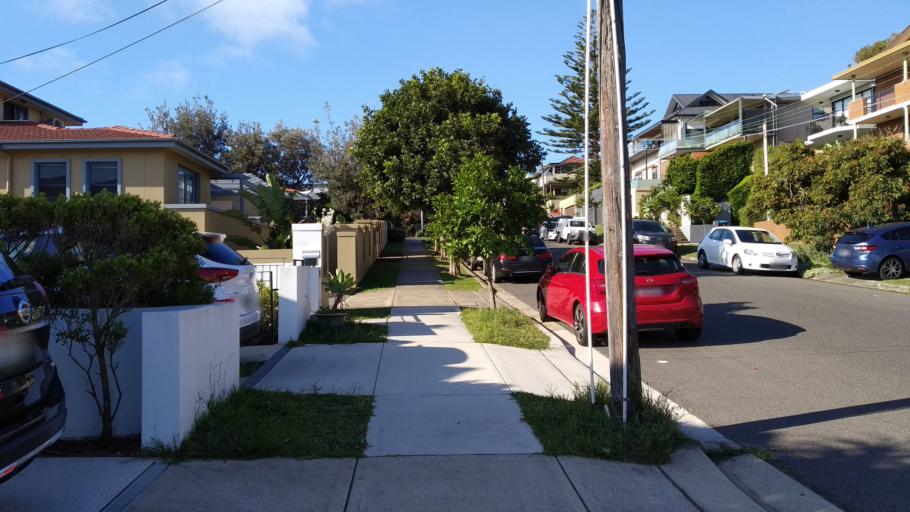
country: AU
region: New South Wales
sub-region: Waverley
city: North Bondi
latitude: -33.8839
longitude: 151.2810
